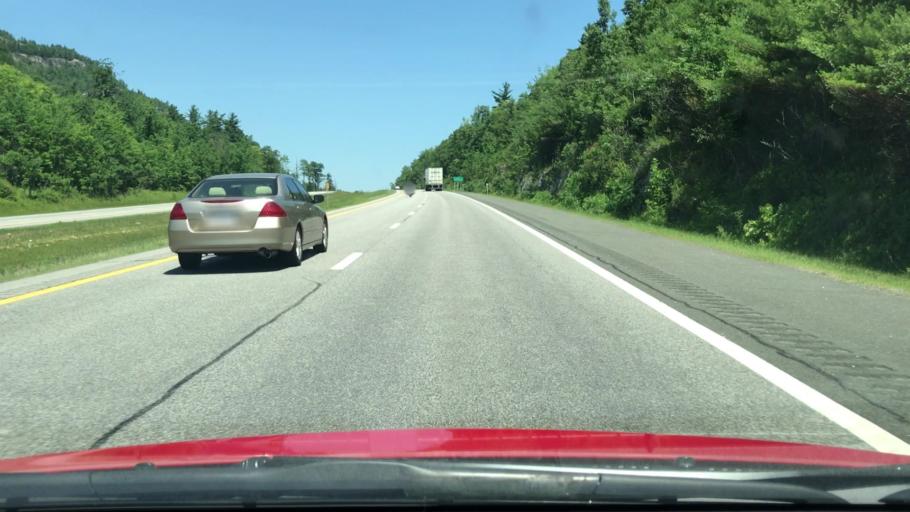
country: US
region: New York
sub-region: Essex County
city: Keeseville
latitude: 44.3932
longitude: -73.5025
